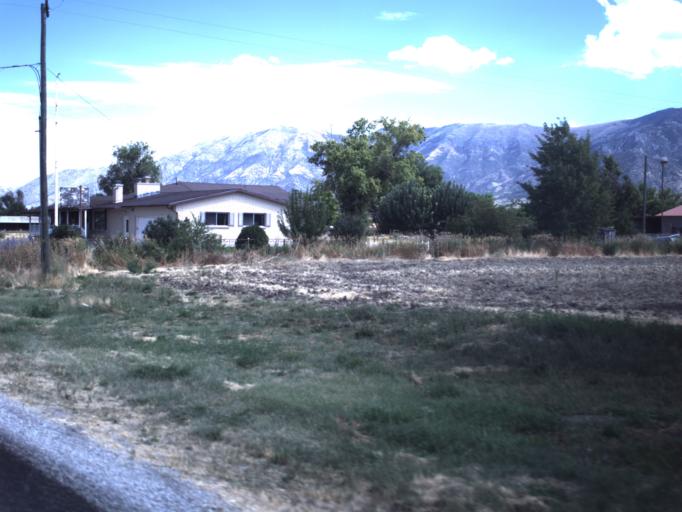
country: US
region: Utah
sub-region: Box Elder County
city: Honeyville
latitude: 41.6017
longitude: -112.1273
